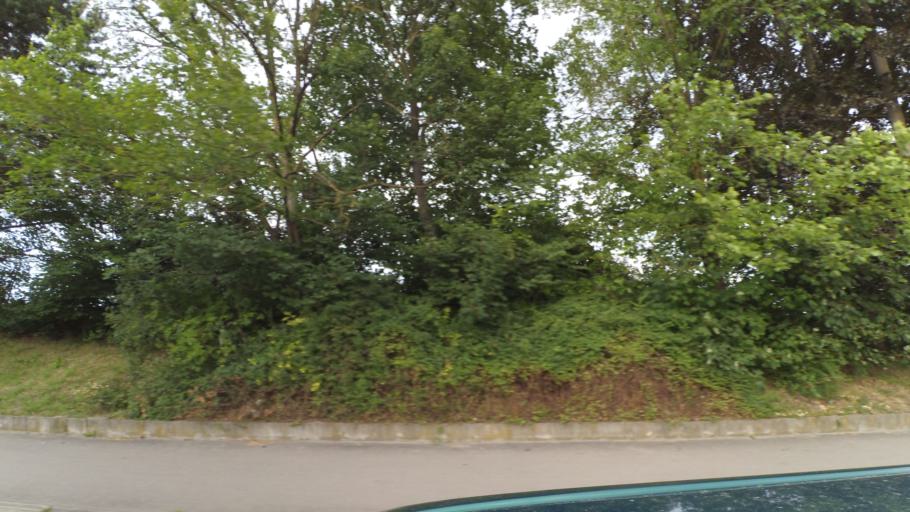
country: DE
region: Bavaria
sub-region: Swabia
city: Hochstadt an der Donau
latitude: 48.6176
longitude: 10.5676
